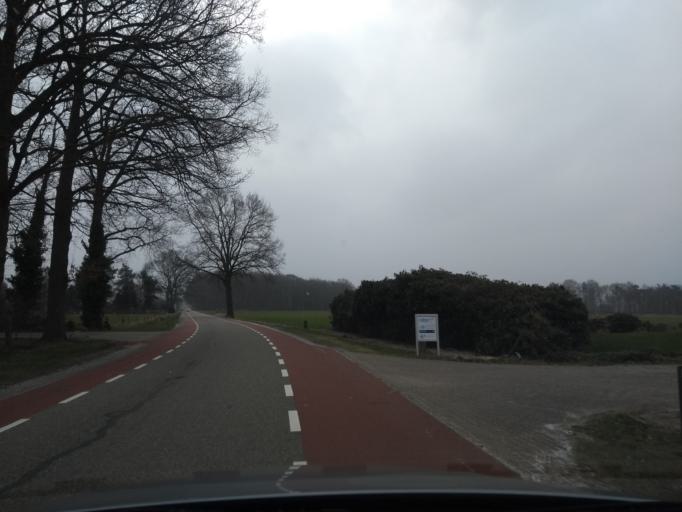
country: NL
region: Overijssel
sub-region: Gemeente Hof van Twente
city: Delden
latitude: 52.2260
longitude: 6.6939
